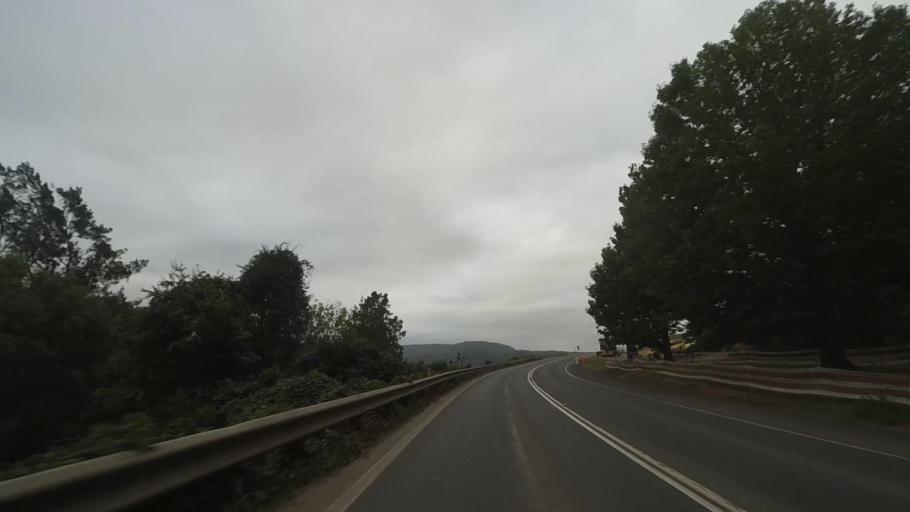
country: AU
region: New South Wales
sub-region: Shoalhaven Shire
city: Berry
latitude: -34.7725
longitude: 150.7057
